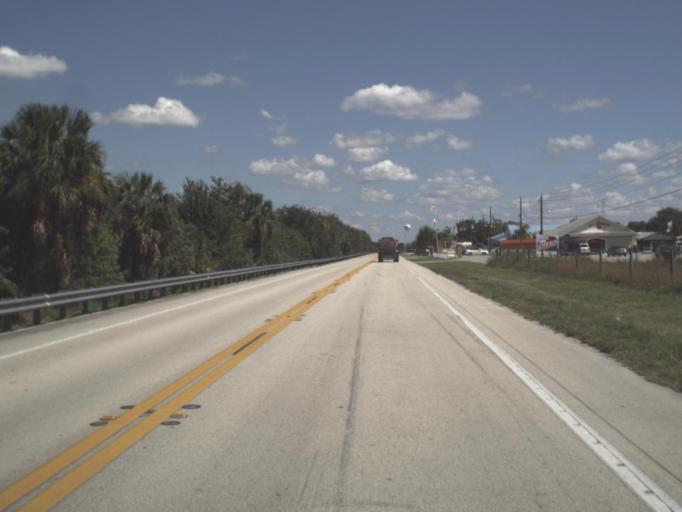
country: US
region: Florida
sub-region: Glades County
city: Buckhead Ridge
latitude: 27.1354
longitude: -80.8941
